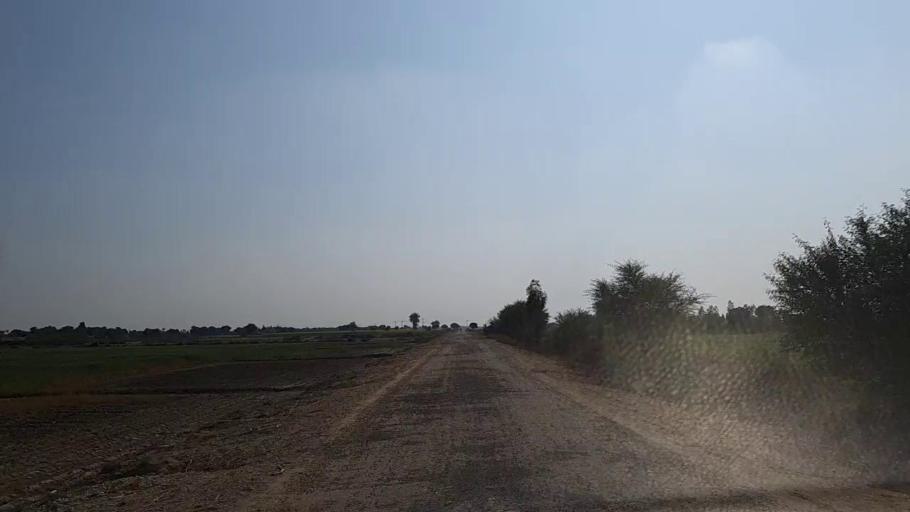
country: PK
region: Sindh
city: Jam Sahib
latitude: 26.2663
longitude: 68.5672
